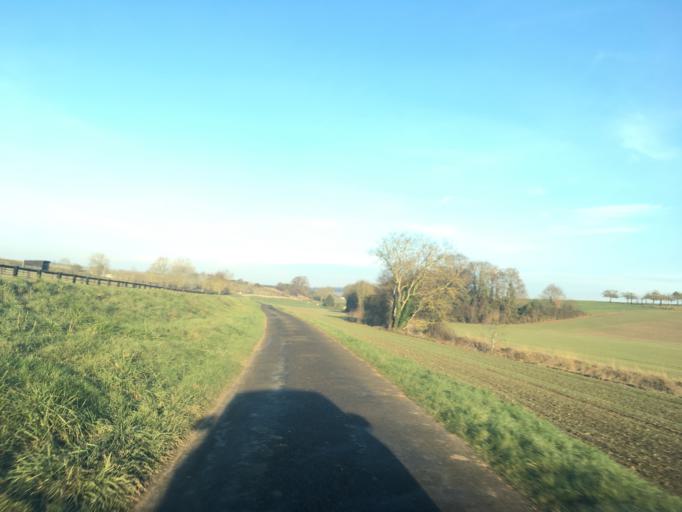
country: FR
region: Haute-Normandie
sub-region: Departement de l'Eure
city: Menilles
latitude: 49.0493
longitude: 1.2924
